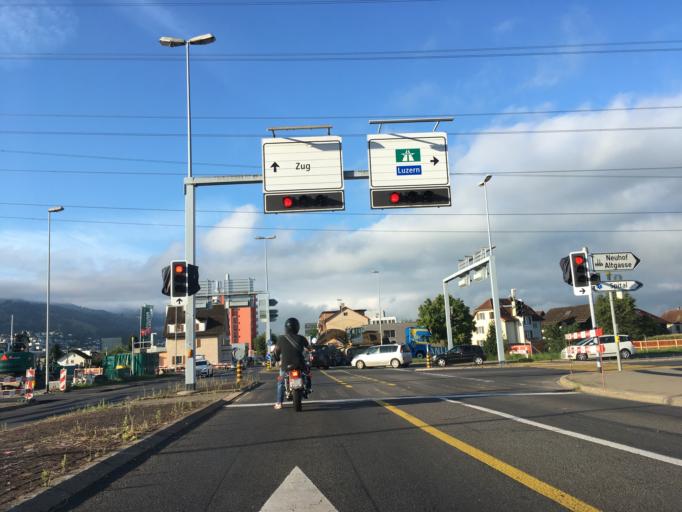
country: CH
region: Zug
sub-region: Zug
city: Baar
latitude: 47.1889
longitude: 8.5217
